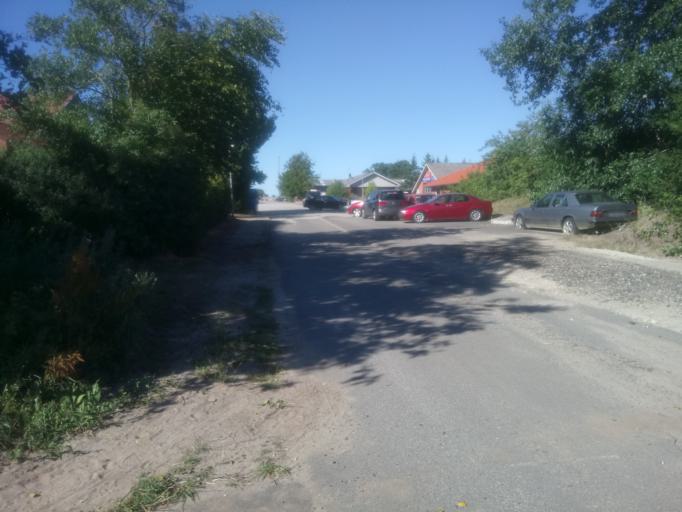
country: DK
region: Central Jutland
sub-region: Herning Kommune
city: Herning
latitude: 56.1524
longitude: 8.9780
